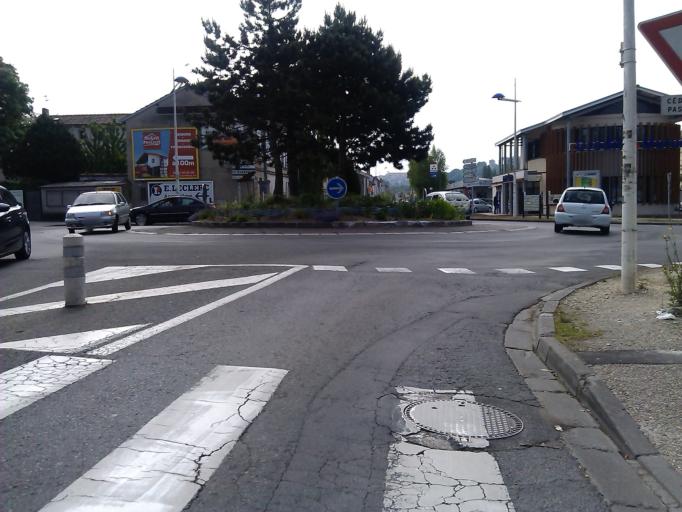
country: FR
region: Poitou-Charentes
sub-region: Departement de la Charente
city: Angouleme
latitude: 45.6594
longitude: 0.1423
